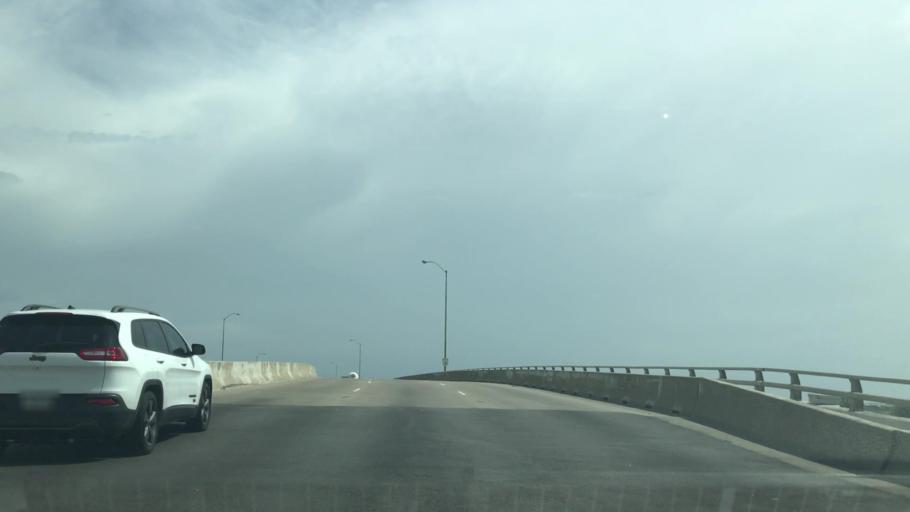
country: US
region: Texas
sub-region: Dallas County
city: Cockrell Hill
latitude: 32.8021
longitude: -96.8738
